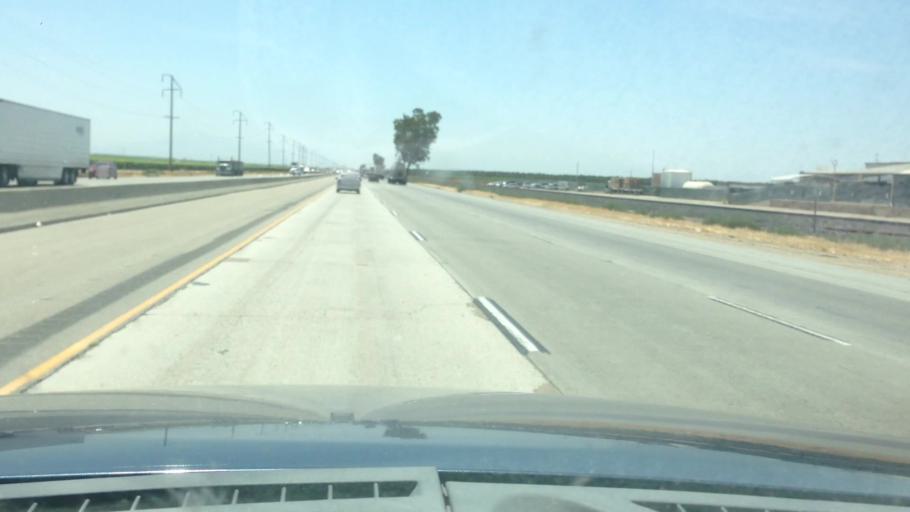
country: US
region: California
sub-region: Kern County
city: Rosedale
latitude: 35.4853
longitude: -119.1456
